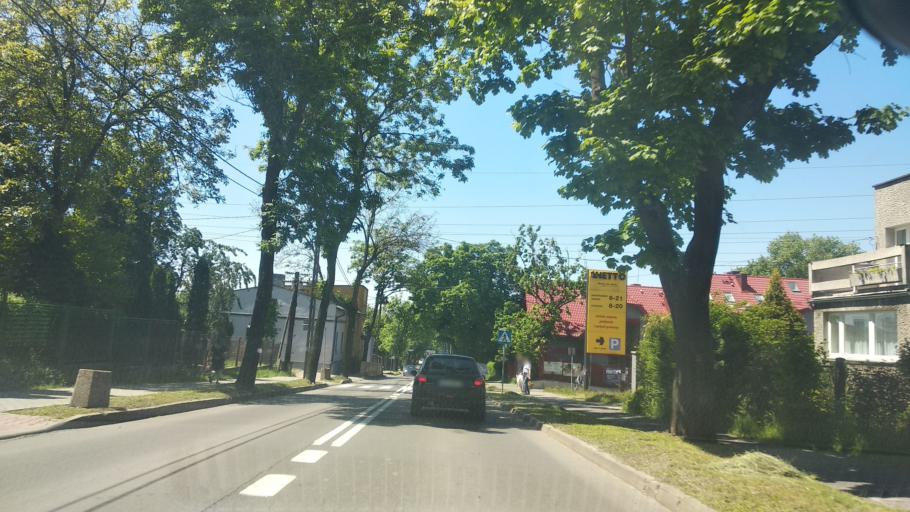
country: PL
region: Silesian Voivodeship
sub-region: Swietochlowice
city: Swietochlowice
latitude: 50.2525
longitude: 18.9076
